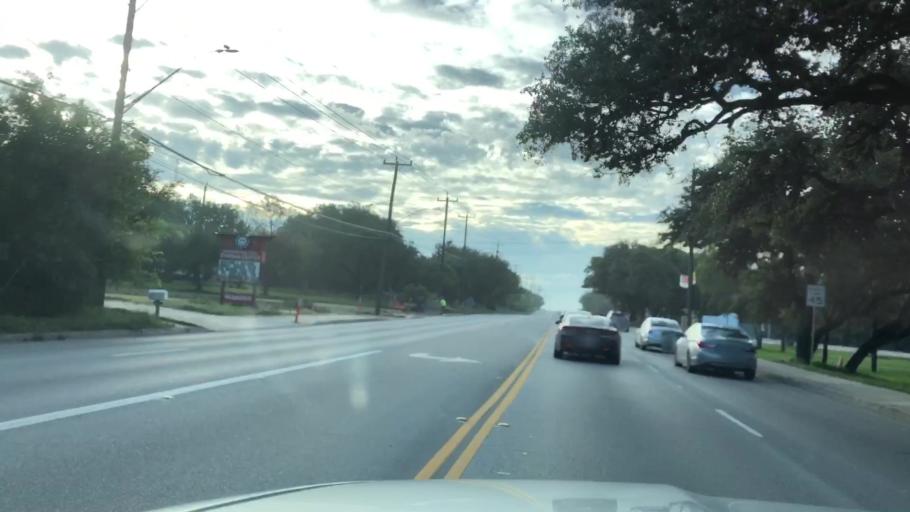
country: US
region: Texas
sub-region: Bexar County
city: Leon Valley
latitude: 29.5335
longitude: -98.6060
